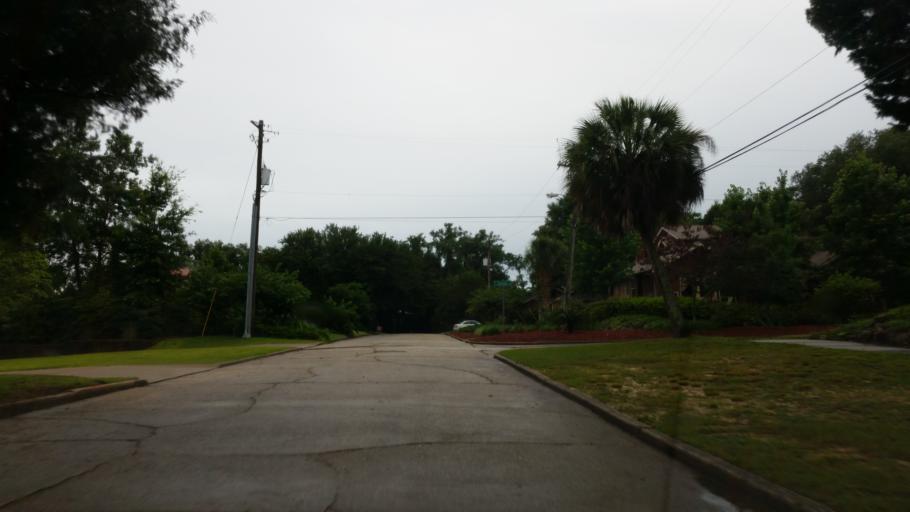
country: US
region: Florida
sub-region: Escambia County
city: East Pensacola Heights
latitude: 30.4243
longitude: -87.1905
